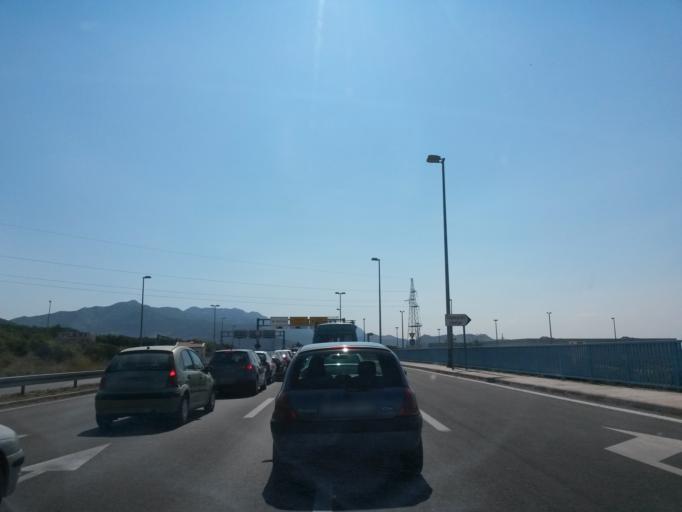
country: HR
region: Splitsko-Dalmatinska
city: Vranjic
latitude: 43.5455
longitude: 16.4499
